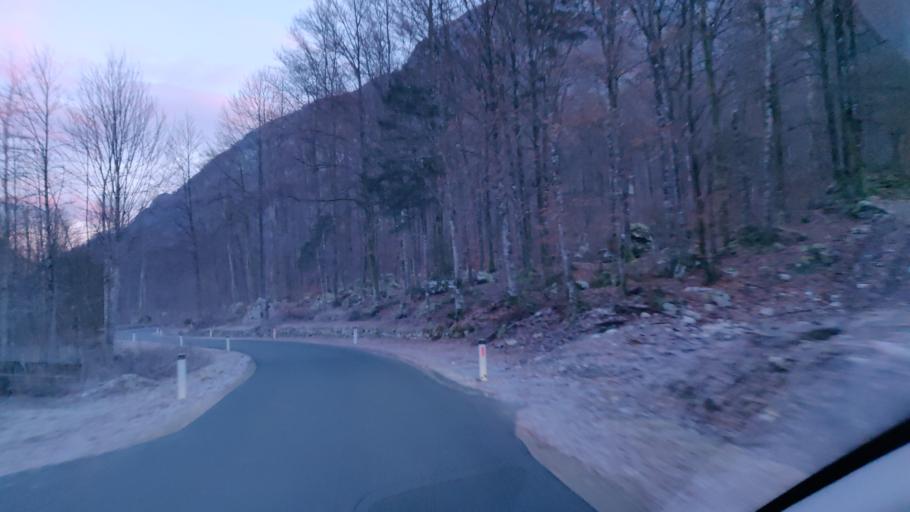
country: SI
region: Tolmin
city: Tolmin
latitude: 46.2770
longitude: 13.8185
